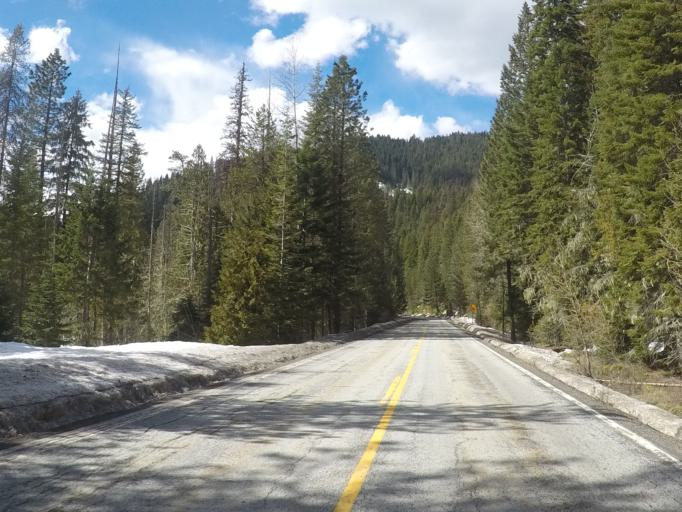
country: US
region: Montana
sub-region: Mineral County
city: Superior
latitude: 46.4770
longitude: -114.8786
